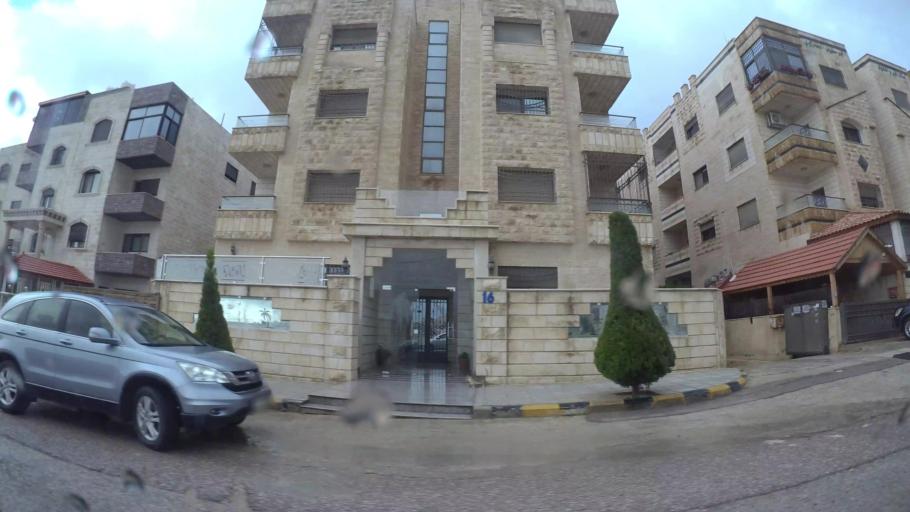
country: JO
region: Amman
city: Al Jubayhah
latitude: 32.0375
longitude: 35.8874
